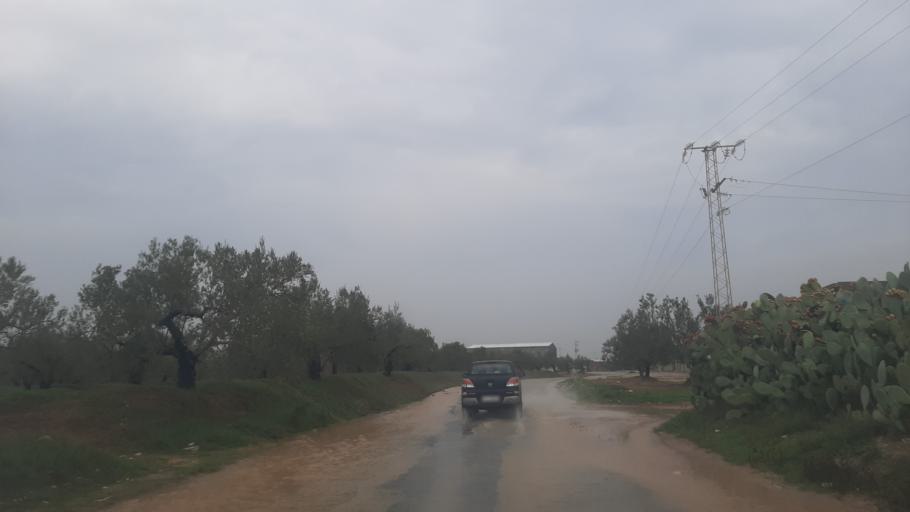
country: TN
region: Al Munastir
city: Sidi Bin Nur
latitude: 35.4726
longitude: 10.8825
